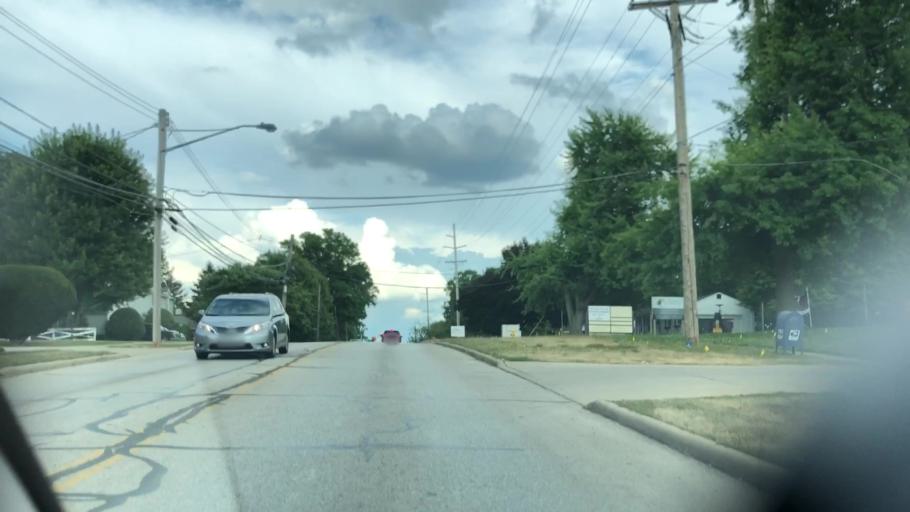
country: US
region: Ohio
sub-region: Summit County
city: Barberton
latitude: 41.0104
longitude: -81.5853
